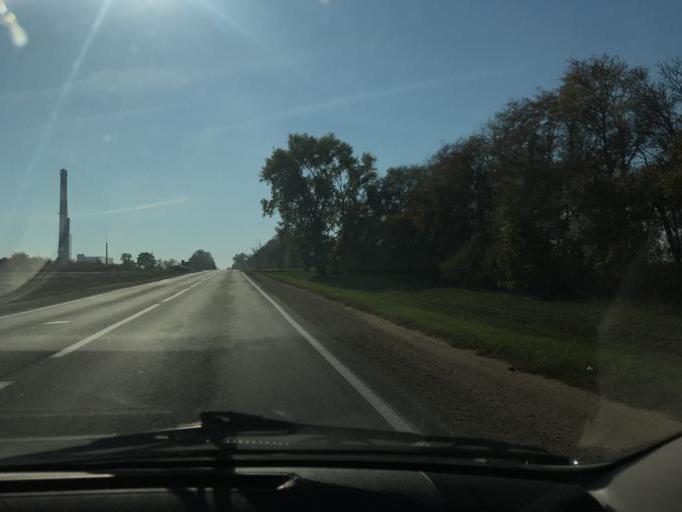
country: BY
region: Minsk
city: Starobin
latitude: 52.8017
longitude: 27.4647
